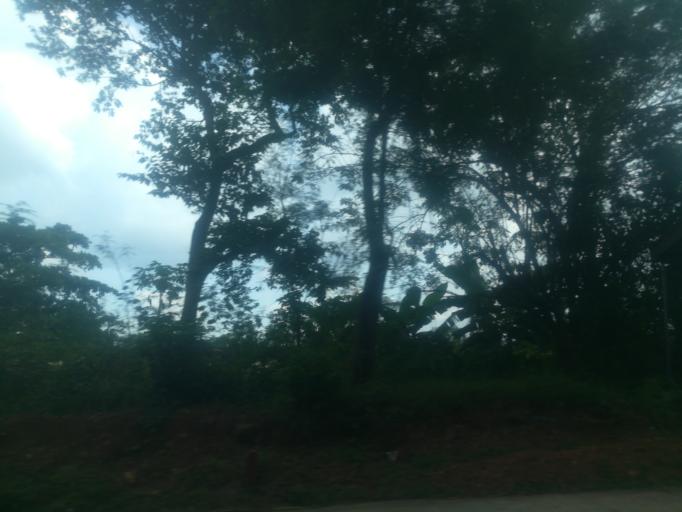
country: NG
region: Oyo
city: Ibadan
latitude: 7.4412
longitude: 3.8939
